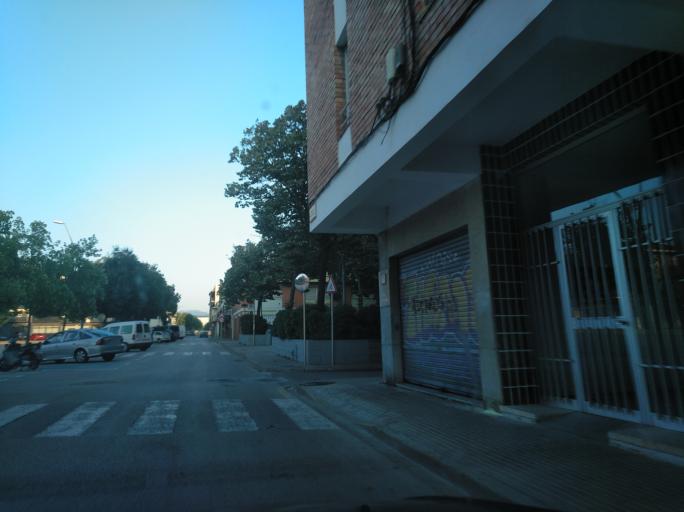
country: ES
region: Catalonia
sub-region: Provincia de Girona
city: Salt
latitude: 41.9707
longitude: 2.7891
